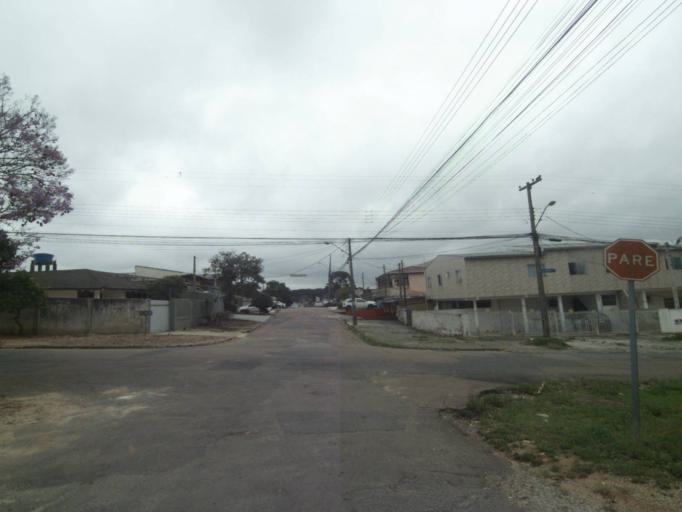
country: BR
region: Parana
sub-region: Sao Jose Dos Pinhais
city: Sao Jose dos Pinhais
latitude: -25.5422
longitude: -49.2901
